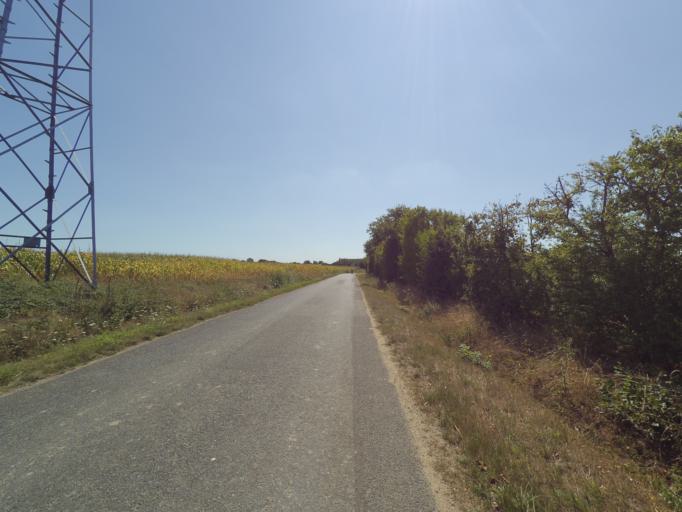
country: FR
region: Pays de la Loire
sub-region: Departement de la Loire-Atlantique
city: Vieillevigne
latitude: 46.9862
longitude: -1.4233
